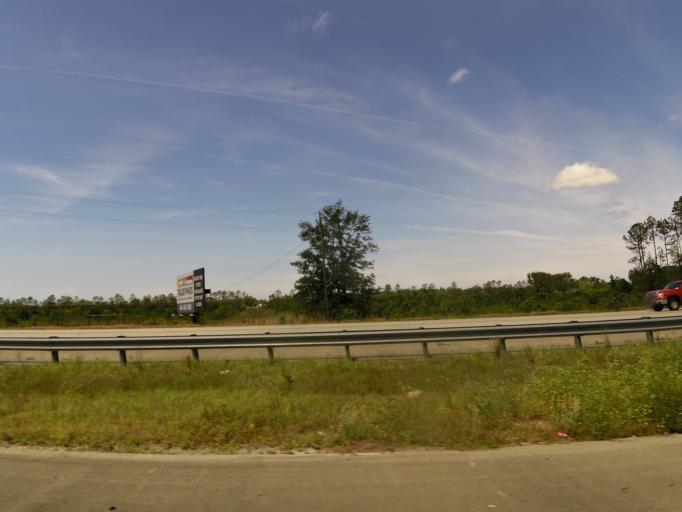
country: US
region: Georgia
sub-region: Glynn County
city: Country Club Estates
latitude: 31.2659
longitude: -81.4933
